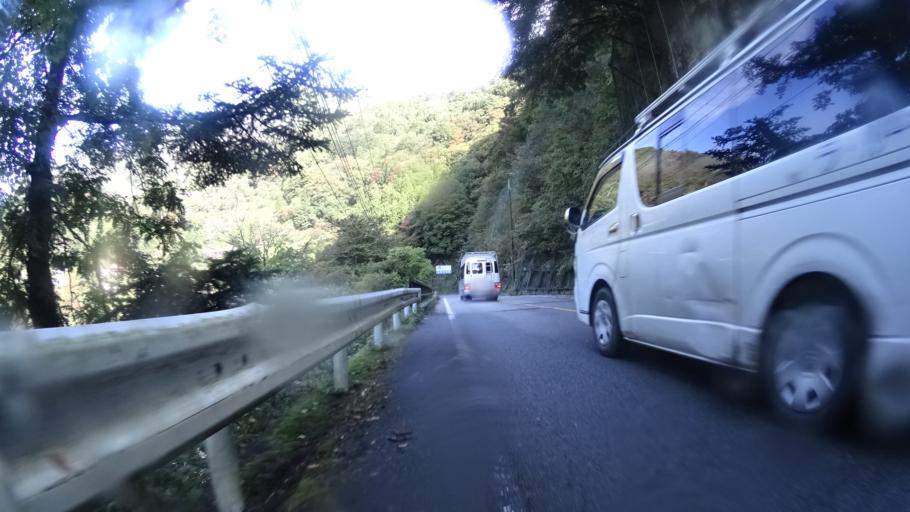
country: JP
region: Yamanashi
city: Otsuki
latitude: 35.7830
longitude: 138.9771
